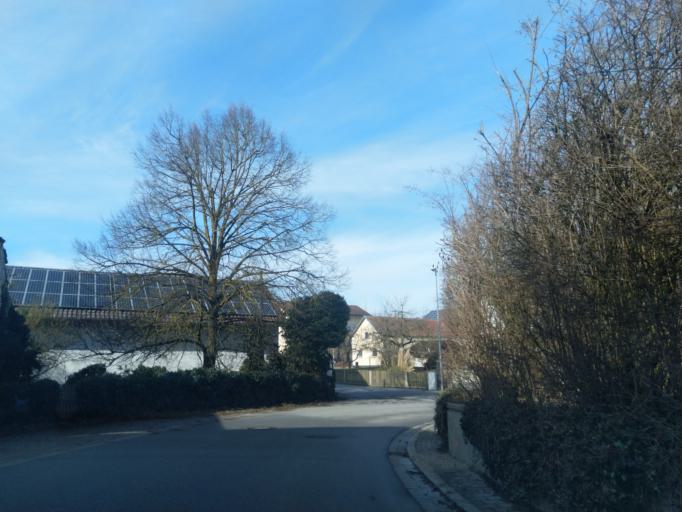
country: DE
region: Bavaria
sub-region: Lower Bavaria
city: Wallerfing
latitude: 48.6809
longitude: 12.8946
